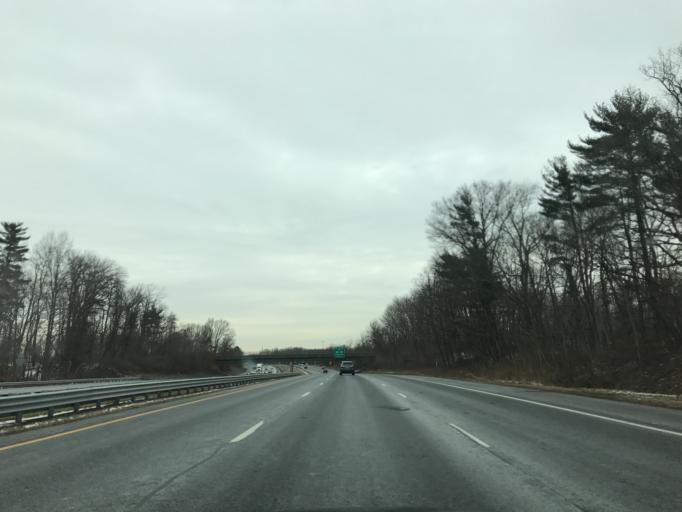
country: US
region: New Jersey
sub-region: Burlington County
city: Bordentown
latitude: 40.1288
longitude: -74.7156
